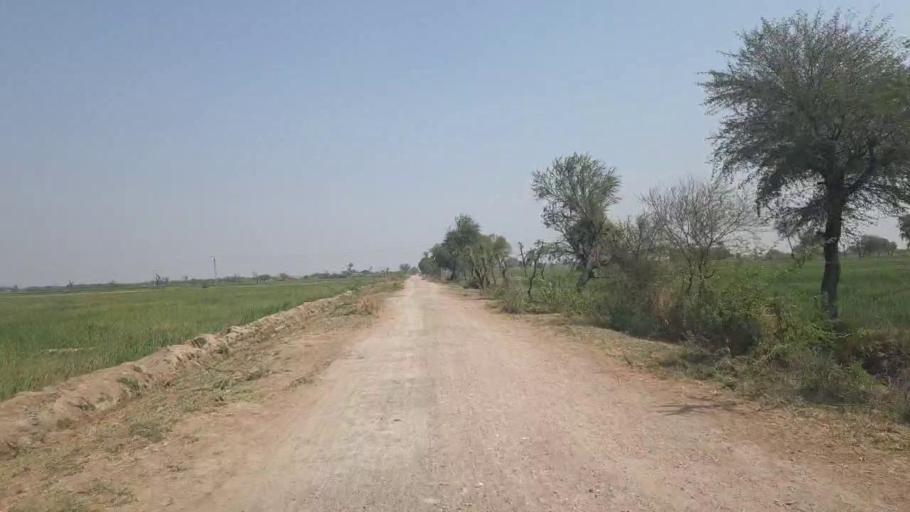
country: PK
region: Sindh
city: Dhoro Naro
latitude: 25.4861
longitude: 69.5555
